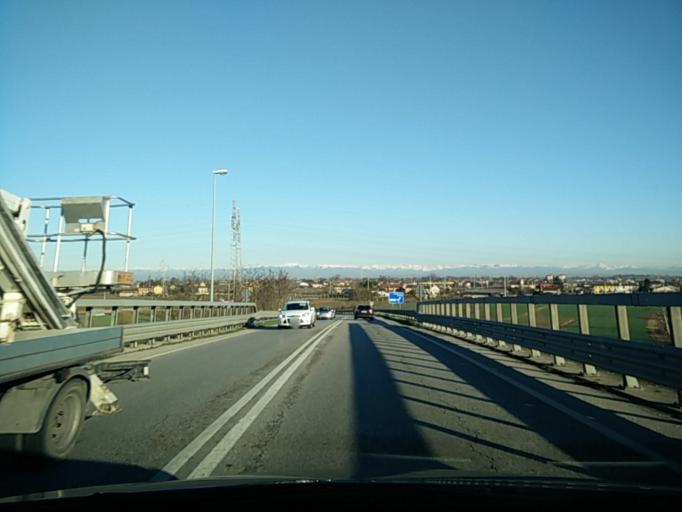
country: IT
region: Veneto
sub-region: Provincia di Venezia
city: Arino
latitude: 45.4495
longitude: 12.0496
